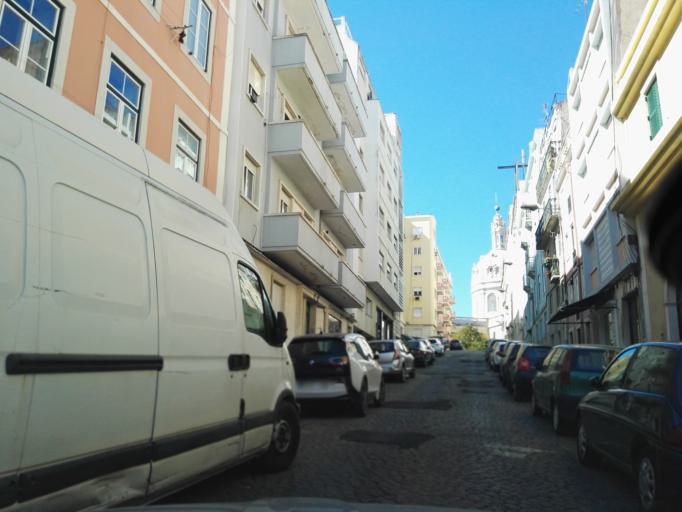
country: PT
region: Lisbon
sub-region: Lisbon
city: Lisbon
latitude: 38.7121
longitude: -9.1590
